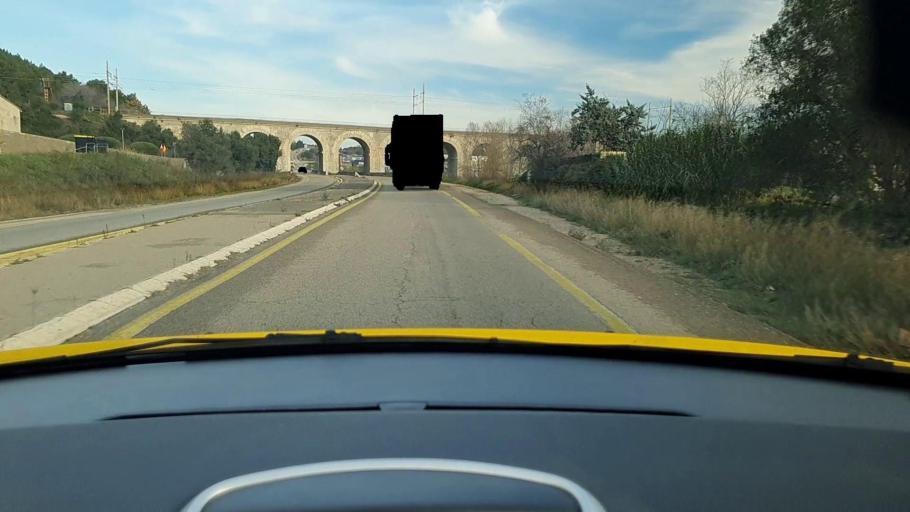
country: FR
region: Languedoc-Roussillon
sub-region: Departement du Gard
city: Beaucaire
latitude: 43.8084
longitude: 4.6106
